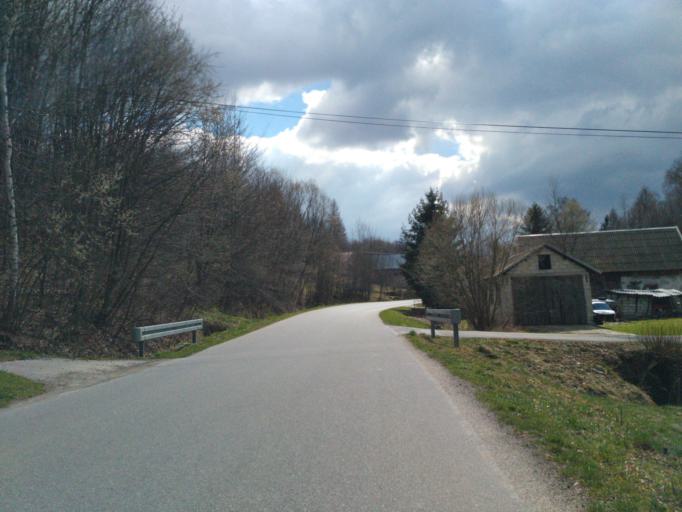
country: PL
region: Subcarpathian Voivodeship
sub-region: Powiat brzozowski
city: Dydnia
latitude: 49.6607
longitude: 22.1984
